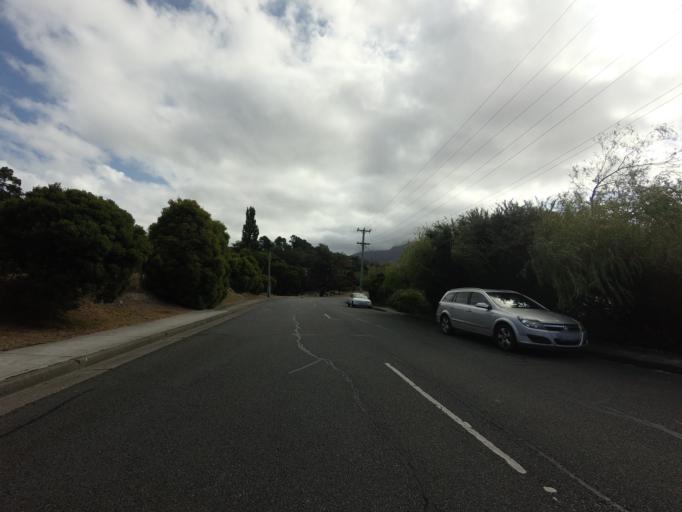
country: AU
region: Tasmania
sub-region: Hobart
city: Dynnyrne
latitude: -42.8977
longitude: 147.2908
